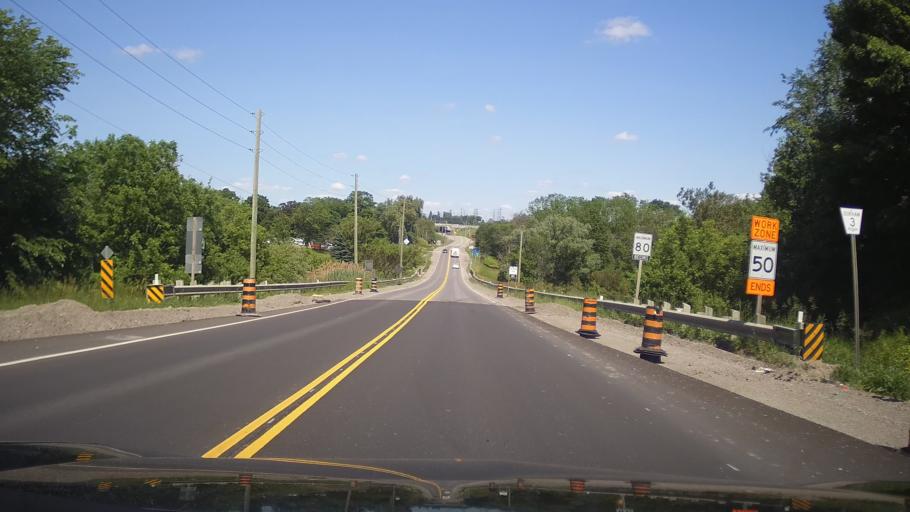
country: CA
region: Ontario
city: Oshawa
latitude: 43.9595
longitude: -78.9334
